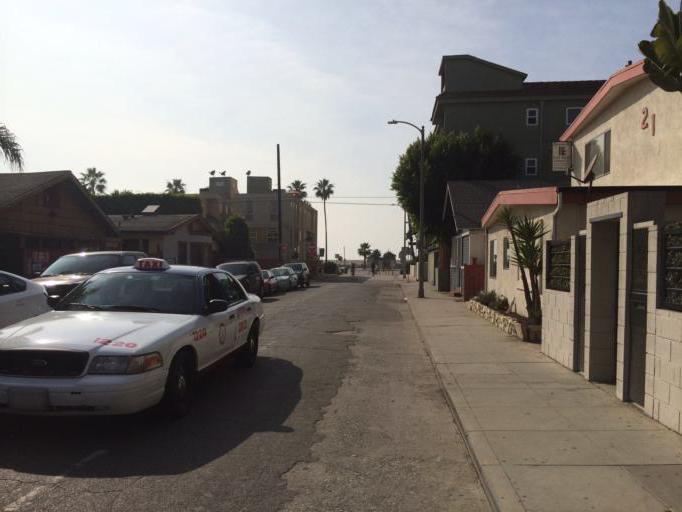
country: US
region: California
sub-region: Los Angeles County
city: Marina del Rey
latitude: 33.9843
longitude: -118.4701
